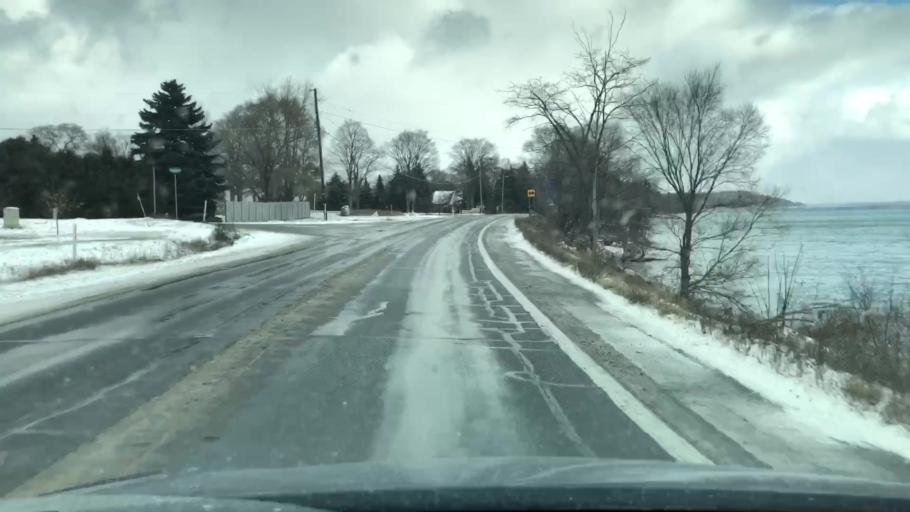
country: US
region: Michigan
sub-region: Grand Traverse County
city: Traverse City
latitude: 44.8182
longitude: -85.5567
